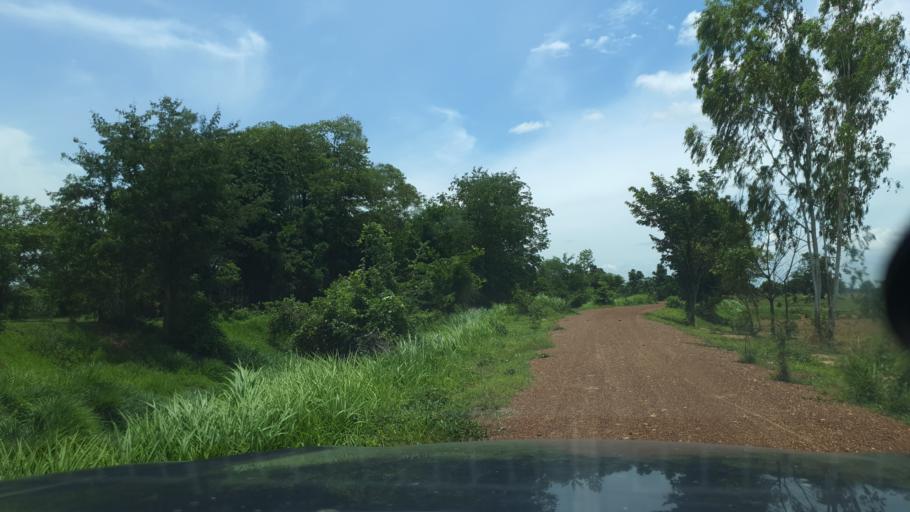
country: TH
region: Sukhothai
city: Ban Na
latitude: 17.0785
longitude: 99.6860
